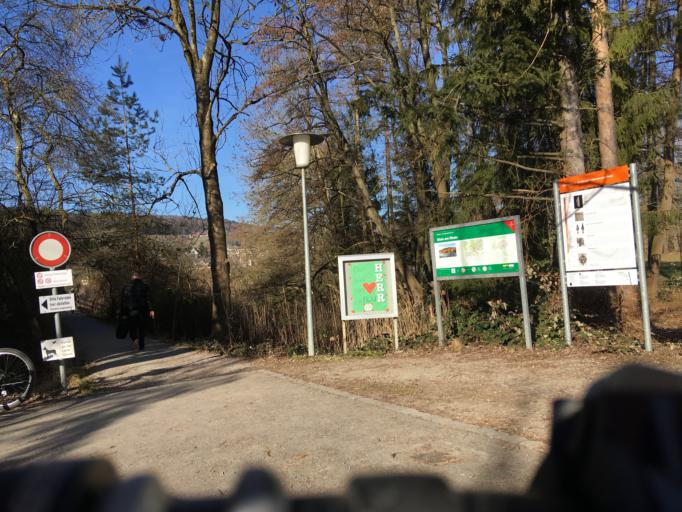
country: CH
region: Thurgau
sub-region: Frauenfeld District
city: Eschenz
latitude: 47.6530
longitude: 8.8672
